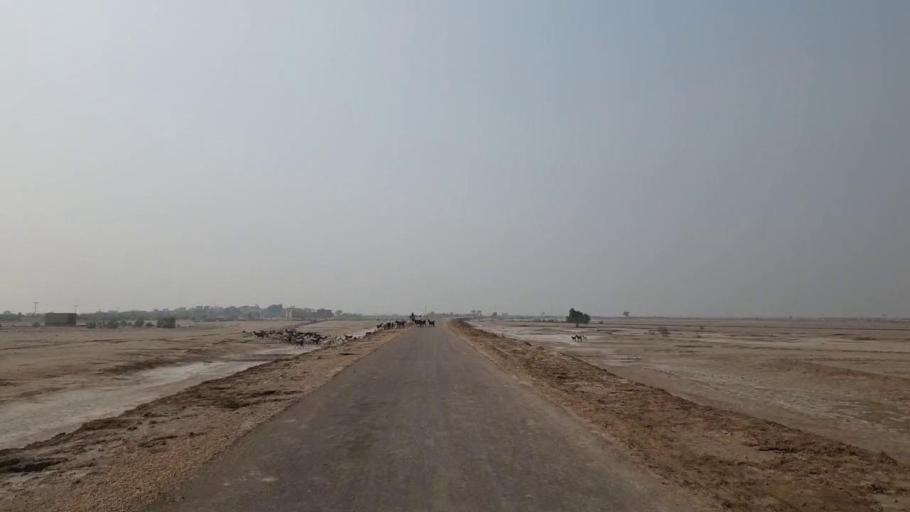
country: PK
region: Sindh
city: Bhan
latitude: 26.5091
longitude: 67.6820
